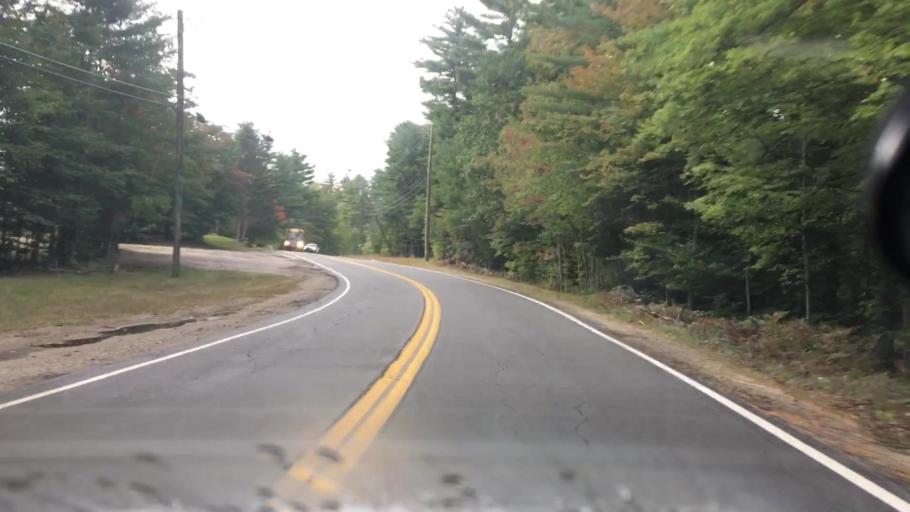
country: US
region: New Hampshire
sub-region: Carroll County
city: Wakefield
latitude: 43.5634
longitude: -71.0284
